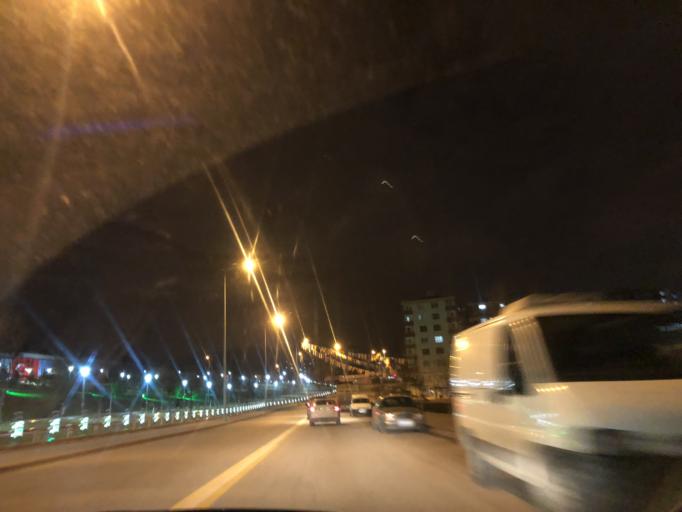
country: TR
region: Ankara
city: Batikent
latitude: 39.9678
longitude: 32.7802
